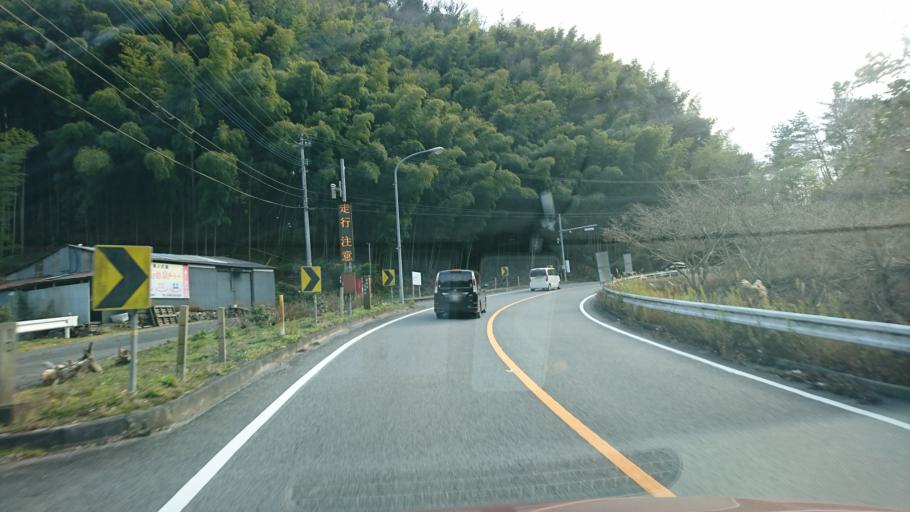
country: JP
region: Ehime
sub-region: Shikoku-chuo Shi
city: Matsuyama
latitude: 33.8950
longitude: 132.8439
